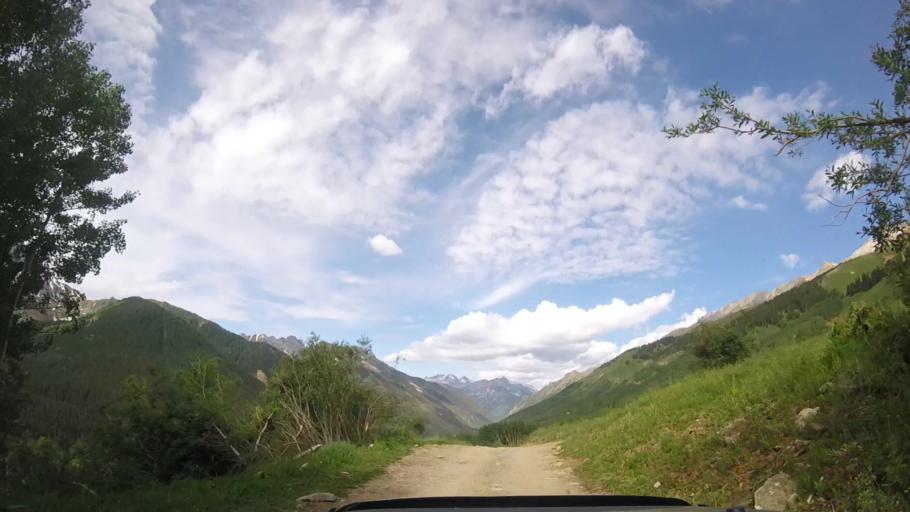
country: US
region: Colorado
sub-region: San Miguel County
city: Telluride
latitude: 37.8598
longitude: -107.7971
